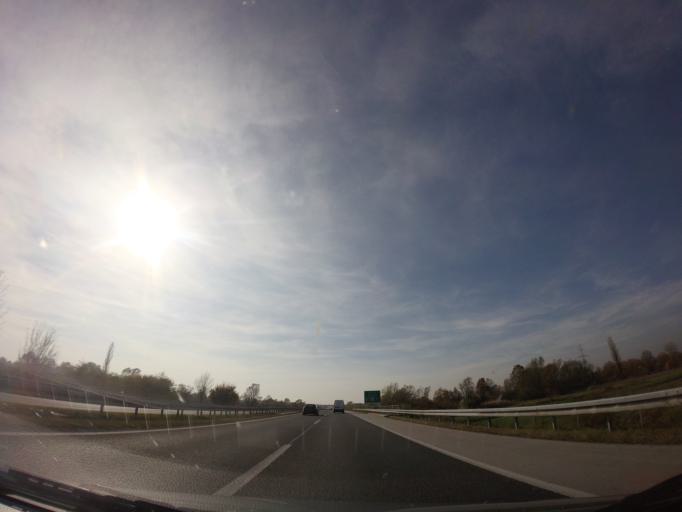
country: HR
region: Zagrebacka
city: Brckovljani
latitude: 45.8771
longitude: 16.2106
